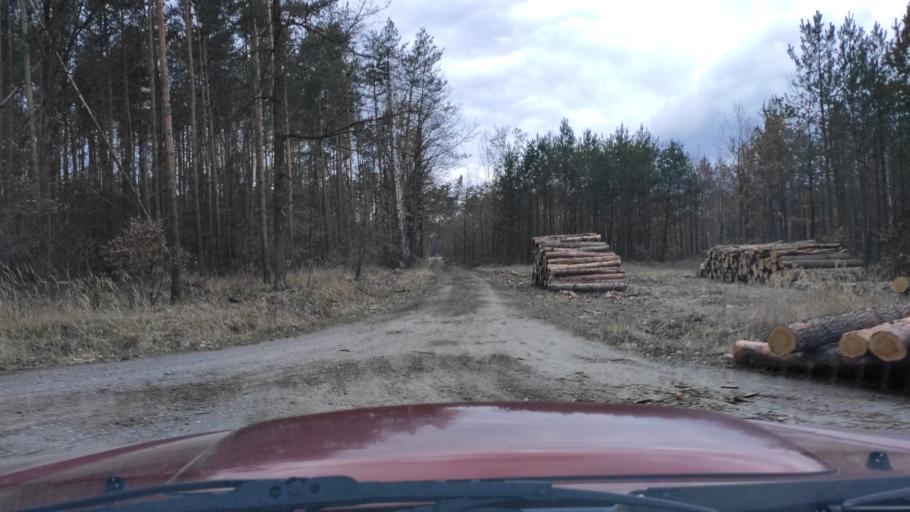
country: PL
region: Masovian Voivodeship
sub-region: Powiat kozienicki
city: Kozienice
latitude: 51.5112
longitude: 21.5432
